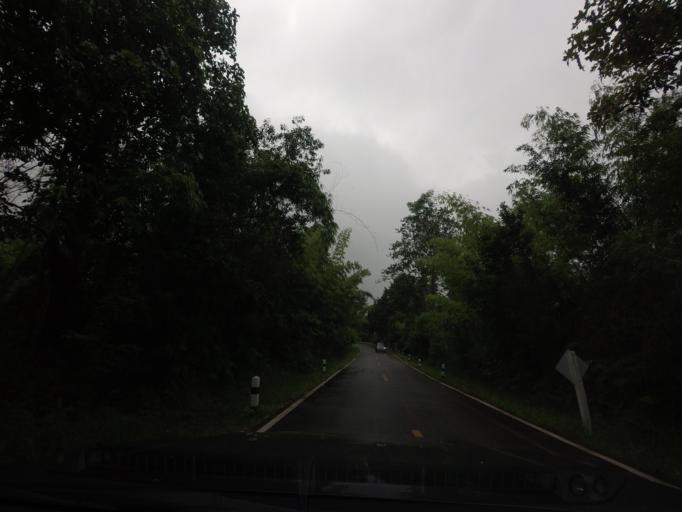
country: TH
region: Nong Khai
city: Sangkhom
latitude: 18.0373
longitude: 102.3333
